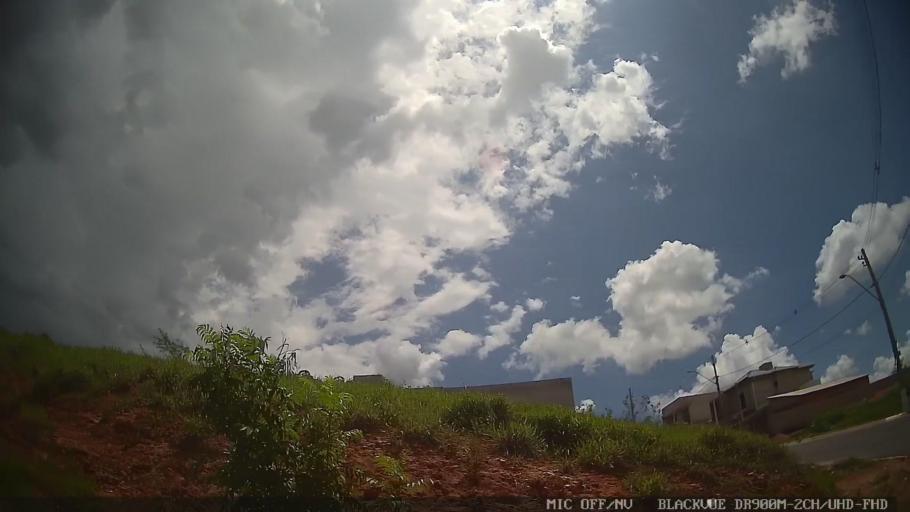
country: BR
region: Sao Paulo
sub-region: Serra Negra
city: Serra Negra
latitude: -22.6008
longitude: -46.7152
